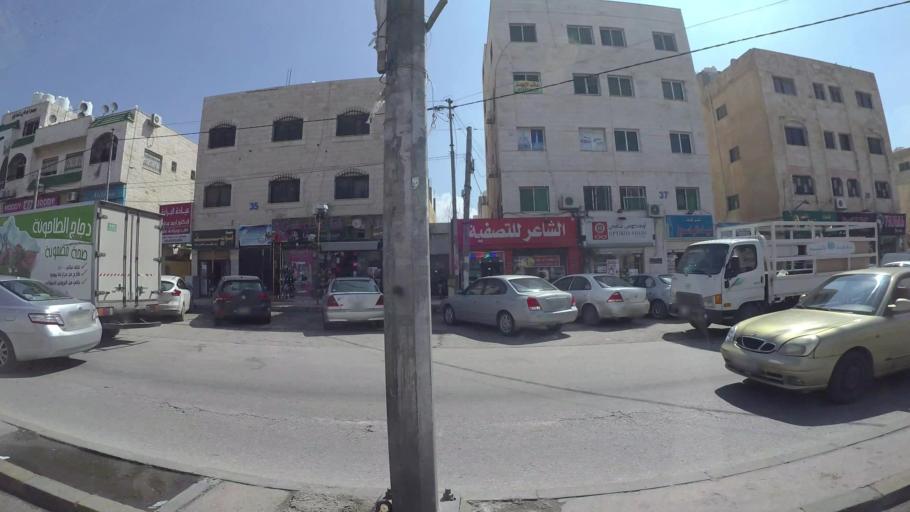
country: JO
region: Amman
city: Al Bunayyat ash Shamaliyah
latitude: 31.9177
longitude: 35.8921
